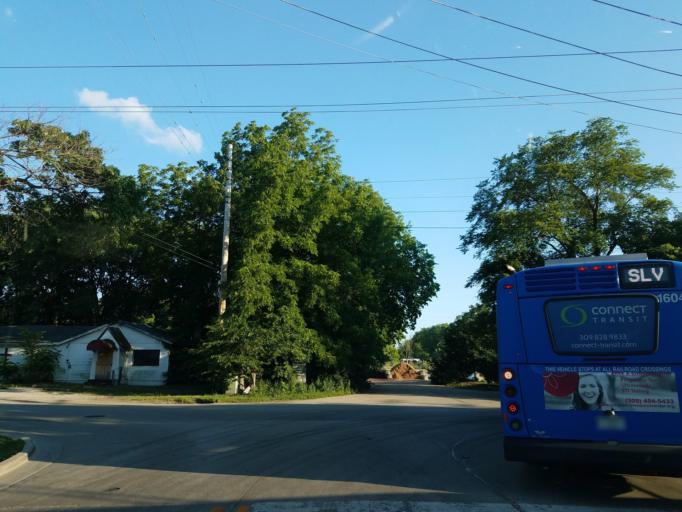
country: US
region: Illinois
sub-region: McLean County
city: Bloomington
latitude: 40.4735
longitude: -89.0163
